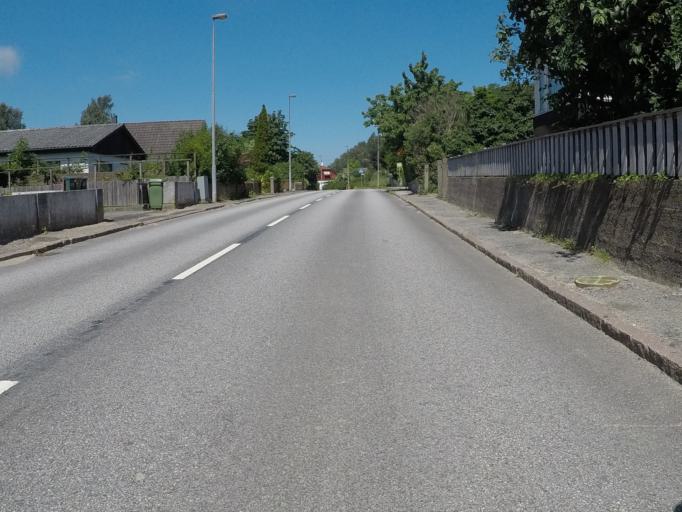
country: SE
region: Skane
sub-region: Malmo
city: Oxie
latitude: 55.5388
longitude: 13.1258
